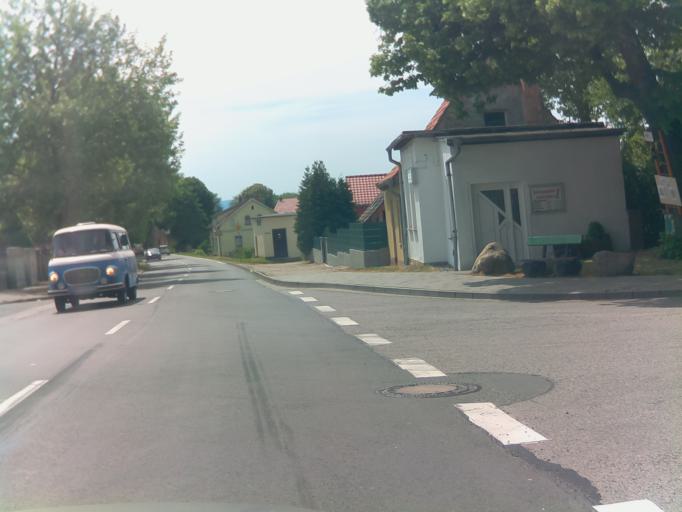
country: DE
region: Saxony-Anhalt
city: Hedersleben
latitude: 51.8583
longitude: 11.2545
